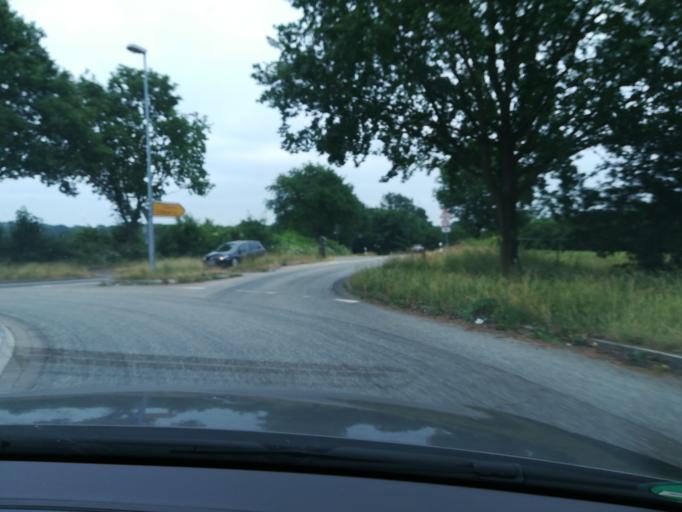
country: DE
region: Schleswig-Holstein
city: Siek
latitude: 53.6335
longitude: 10.3084
